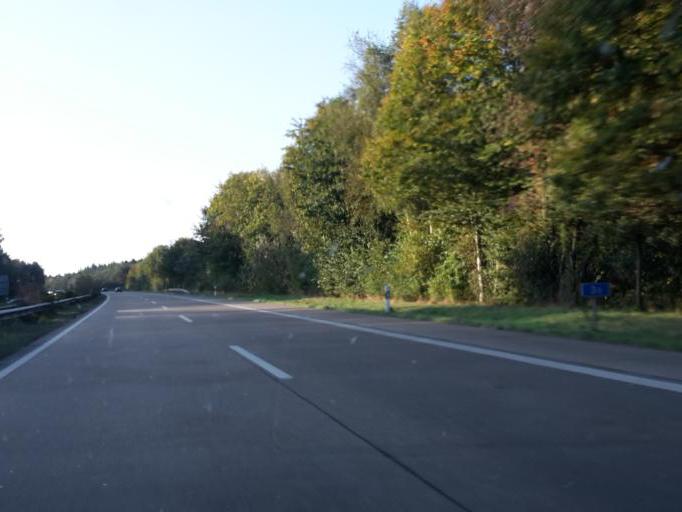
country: DE
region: Lower Saxony
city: Buehren
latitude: 52.8761
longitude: 8.2084
